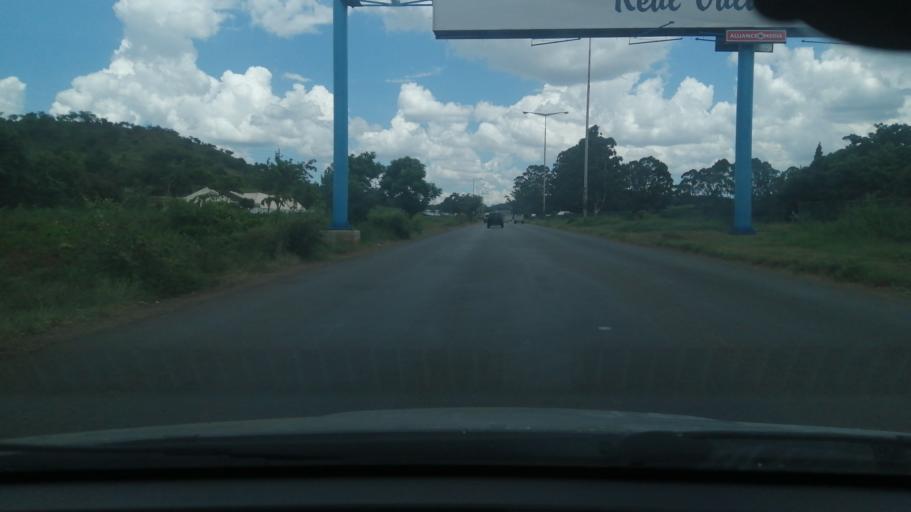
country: ZW
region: Harare
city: Harare
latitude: -17.8248
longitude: 30.9790
